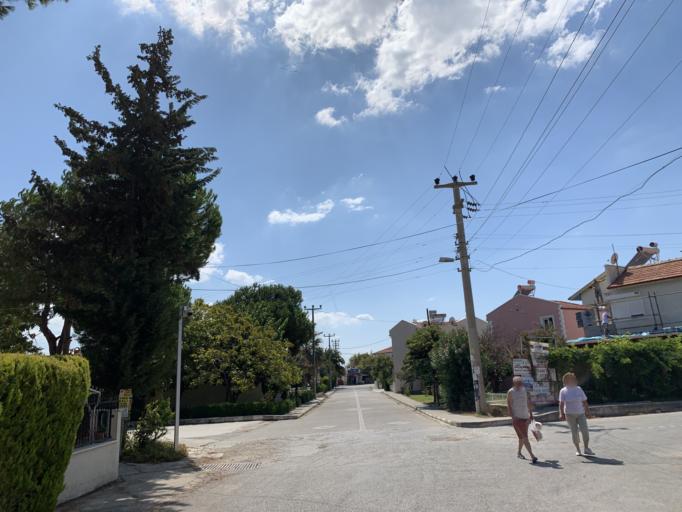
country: TR
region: Balikesir
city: Altinoluk
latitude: 39.5615
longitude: 26.8374
